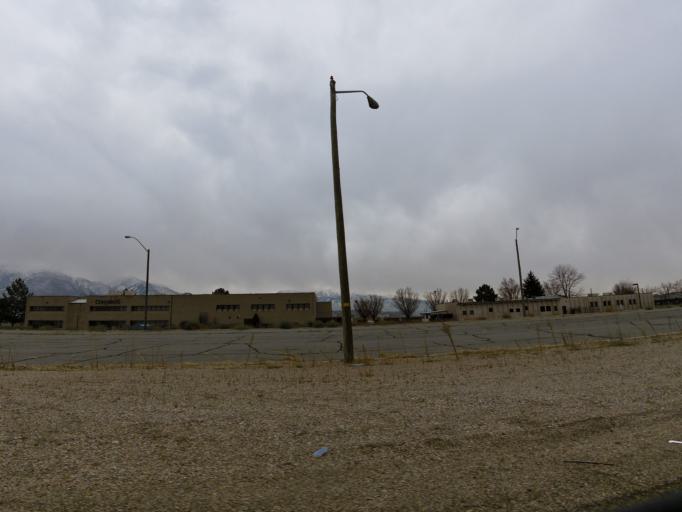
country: US
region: Utah
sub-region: Weber County
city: Riverdale
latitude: 41.1848
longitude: -112.0141
